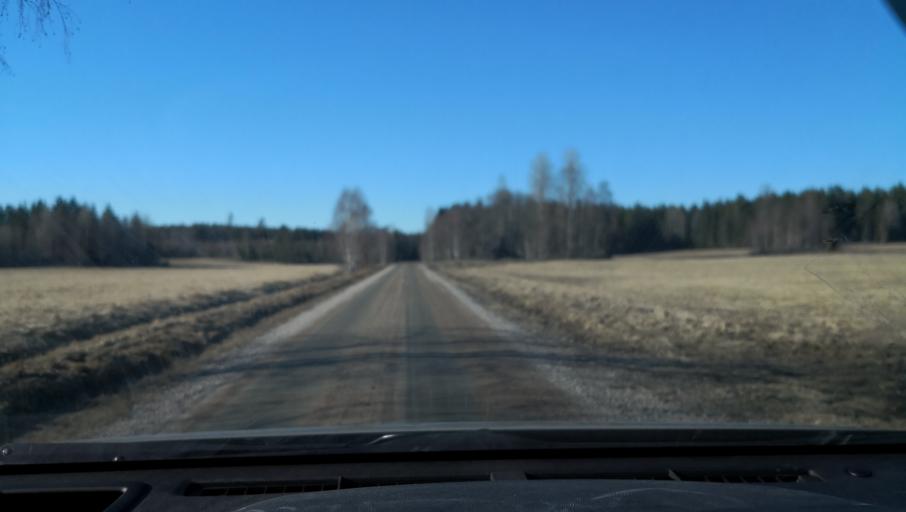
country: SE
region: Vaestmanland
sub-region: Sala Kommun
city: Sala
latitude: 60.1318
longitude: 16.6518
